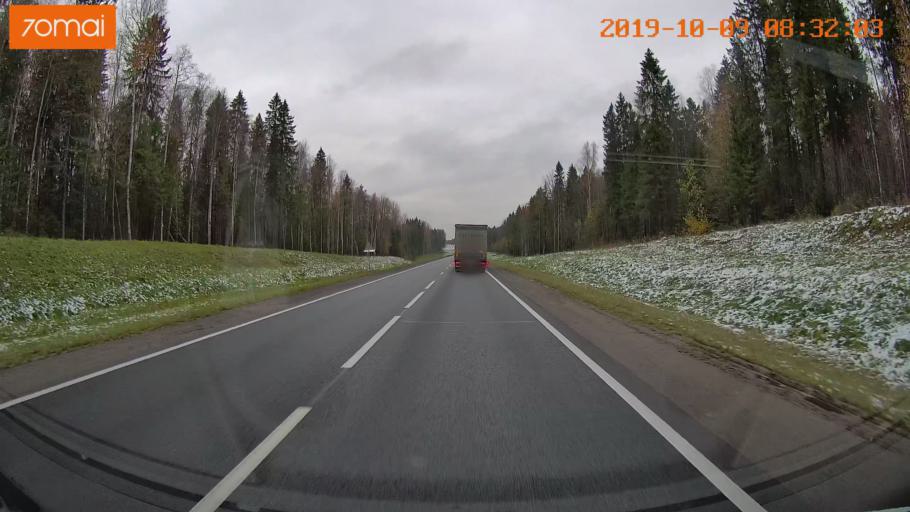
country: RU
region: Vologda
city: Gryazovets
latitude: 58.8617
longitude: 40.1987
